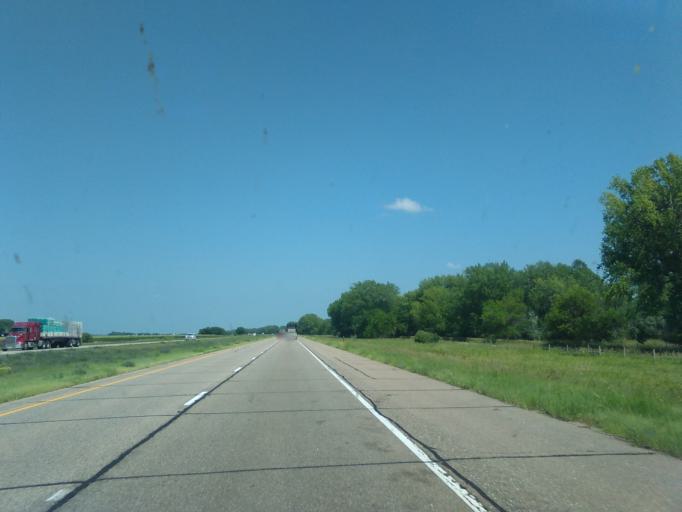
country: US
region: Nebraska
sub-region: Buffalo County
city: Kearney
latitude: 40.6730
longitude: -99.2272
